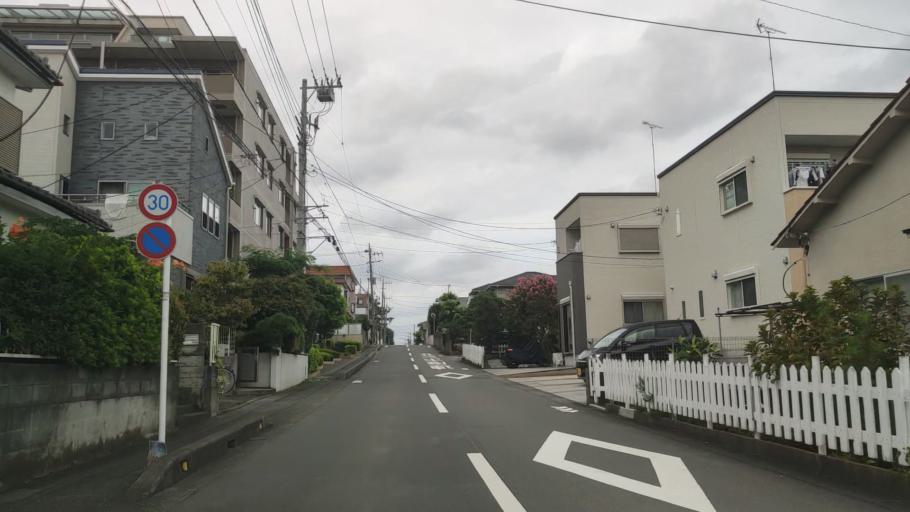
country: JP
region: Kanagawa
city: Minami-rinkan
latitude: 35.5067
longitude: 139.4403
